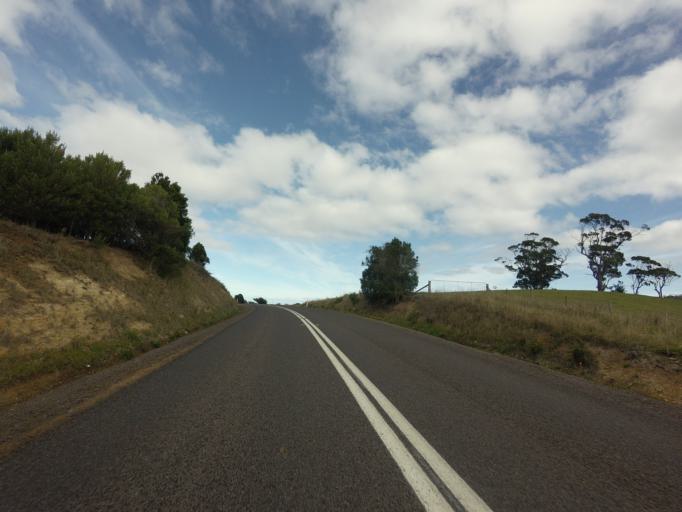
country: AU
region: Tasmania
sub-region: Clarence
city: Sandford
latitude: -43.0671
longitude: 147.7460
